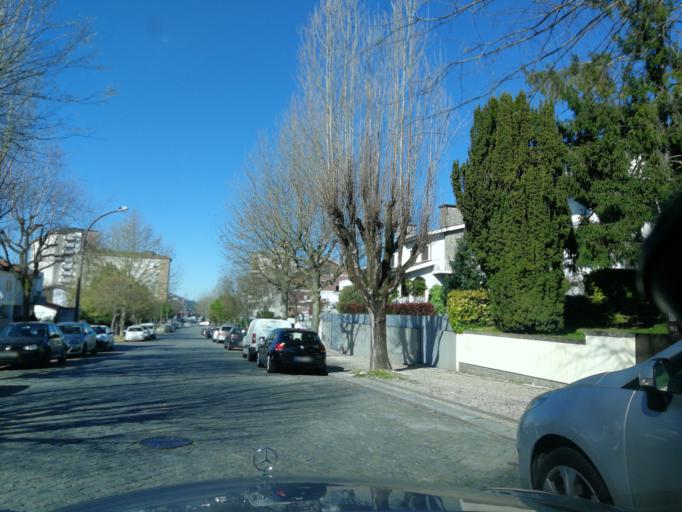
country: PT
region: Braga
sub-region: Braga
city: Braga
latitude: 41.5447
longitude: -8.4291
